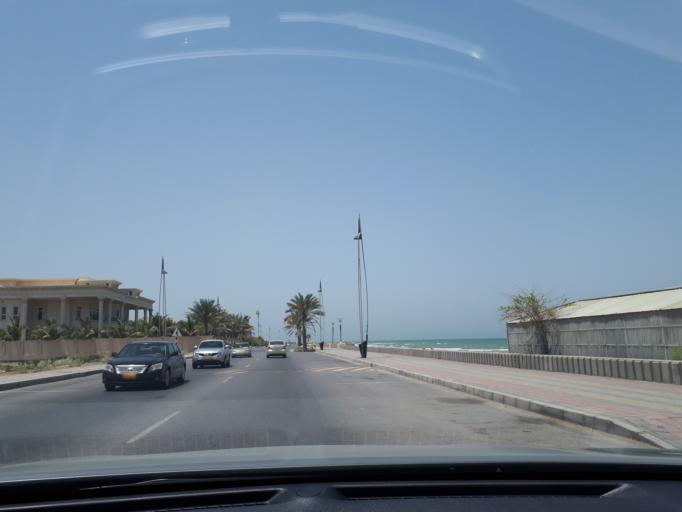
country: OM
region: Muhafazat Masqat
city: As Sib al Jadidah
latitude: 23.6671
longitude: 58.2126
